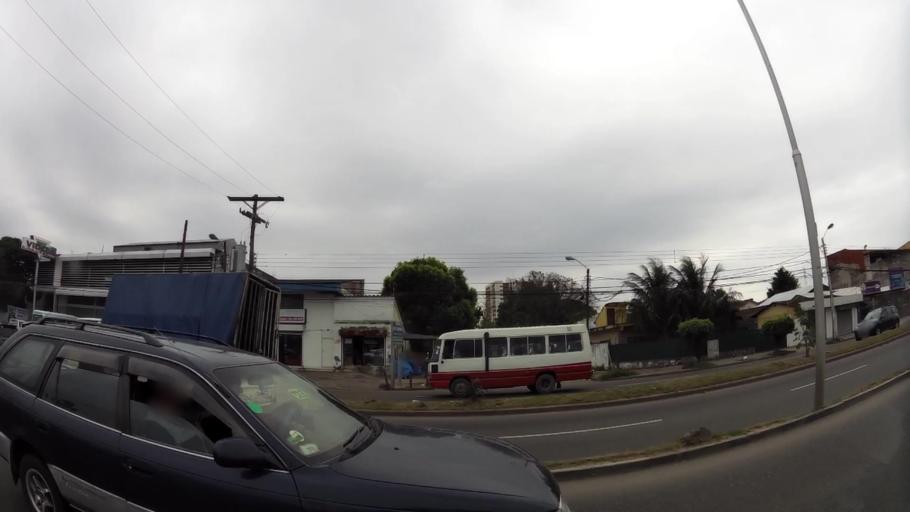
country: BO
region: Santa Cruz
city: Santa Cruz de la Sierra
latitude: -17.7986
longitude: -63.1713
